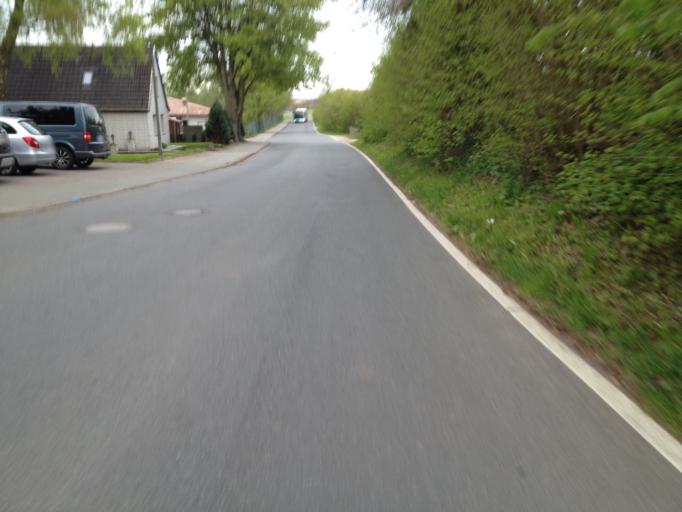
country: DE
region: Schleswig-Holstein
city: Tastrup
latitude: 54.7809
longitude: 9.4662
